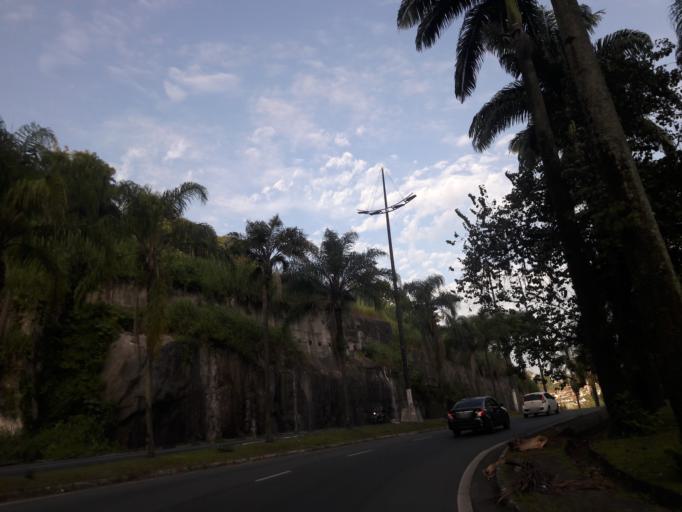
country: BR
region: Sao Paulo
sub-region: Santos
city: Santos
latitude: -23.9370
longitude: -46.3321
